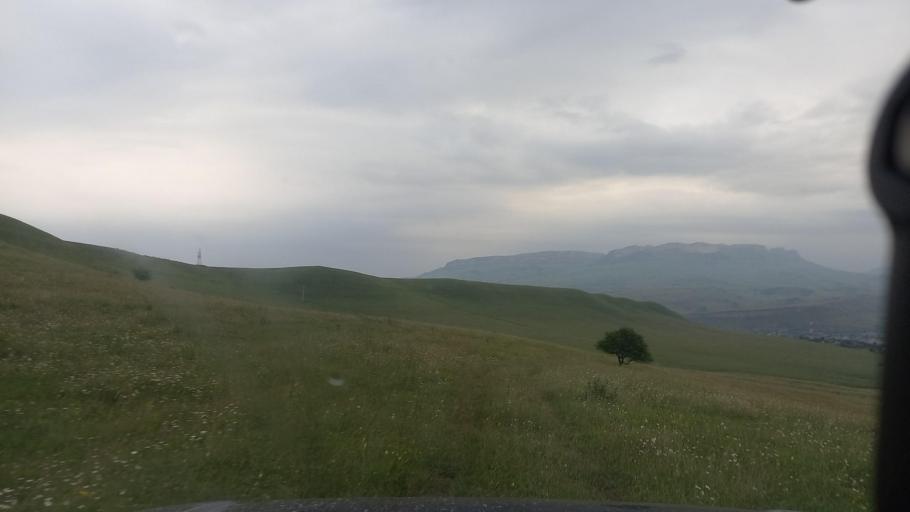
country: RU
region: Karachayevo-Cherkesiya
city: Pregradnaya
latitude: 43.9519
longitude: 41.1579
